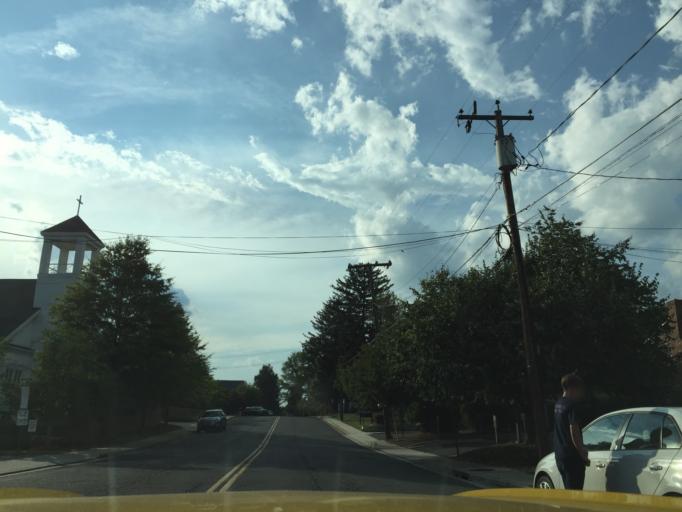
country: US
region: Virginia
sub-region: Fairfax County
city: Vienna
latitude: 38.9038
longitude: -77.2632
